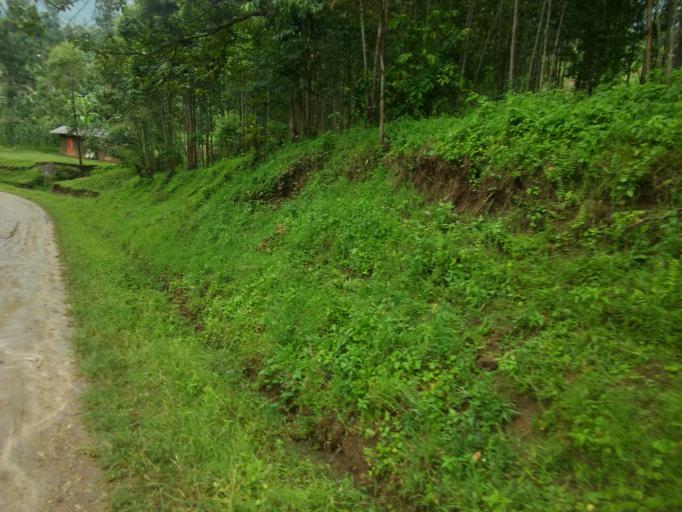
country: UG
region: Eastern Region
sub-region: Mbale District
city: Mbale
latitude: 1.0154
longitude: 34.2242
